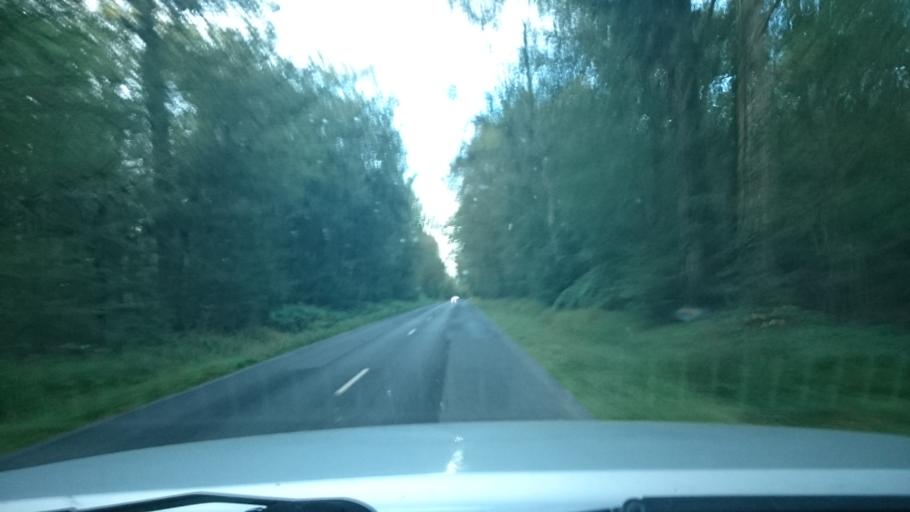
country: FR
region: Ile-de-France
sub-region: Departement de Seine-et-Marne
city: Samois-sur-Seine
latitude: 48.4612
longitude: 2.7298
